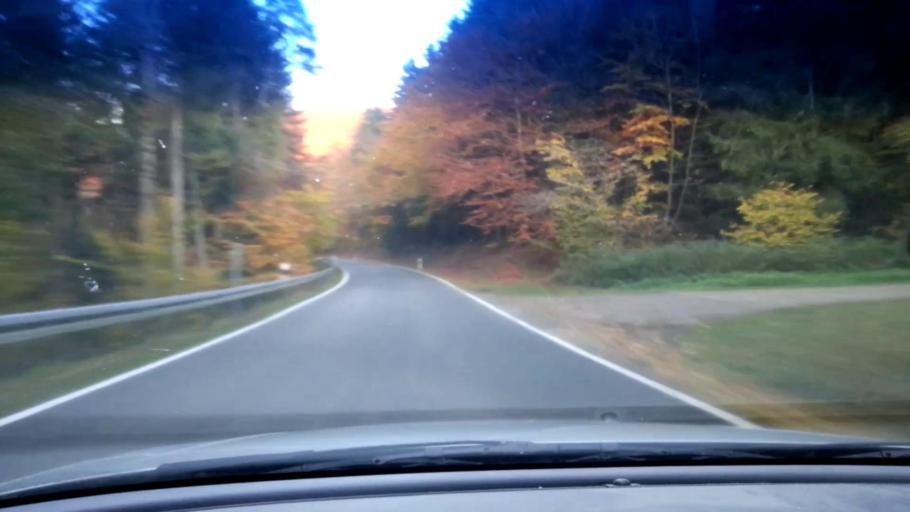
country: DE
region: Bavaria
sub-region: Upper Franconia
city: Heiligenstadt
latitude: 49.8629
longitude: 11.1268
